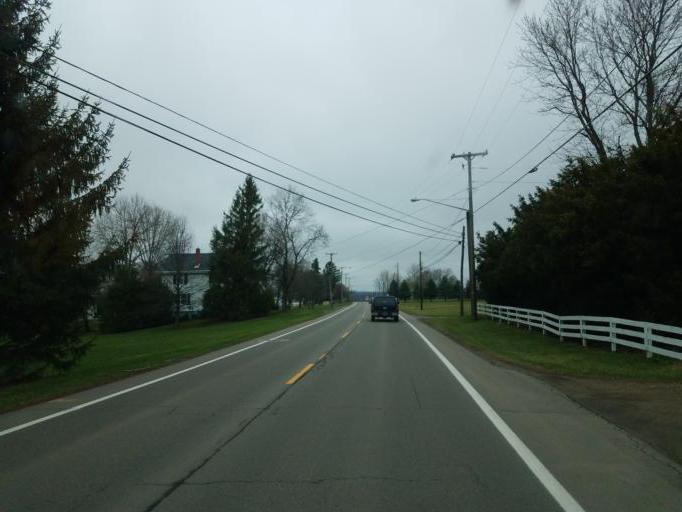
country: US
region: Ohio
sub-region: Ashland County
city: Ashland
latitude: 40.7771
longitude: -82.2621
